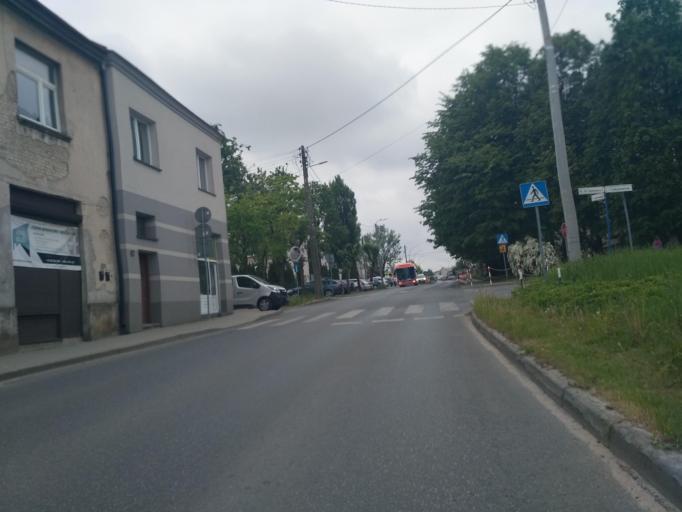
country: PL
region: Subcarpathian Voivodeship
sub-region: Krosno
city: Krosno
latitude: 49.6900
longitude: 21.7608
